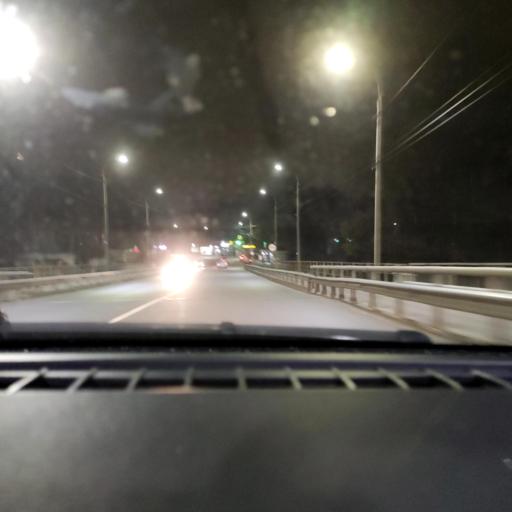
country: RU
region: Voronezj
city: Voronezh
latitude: 51.7252
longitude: 39.2622
